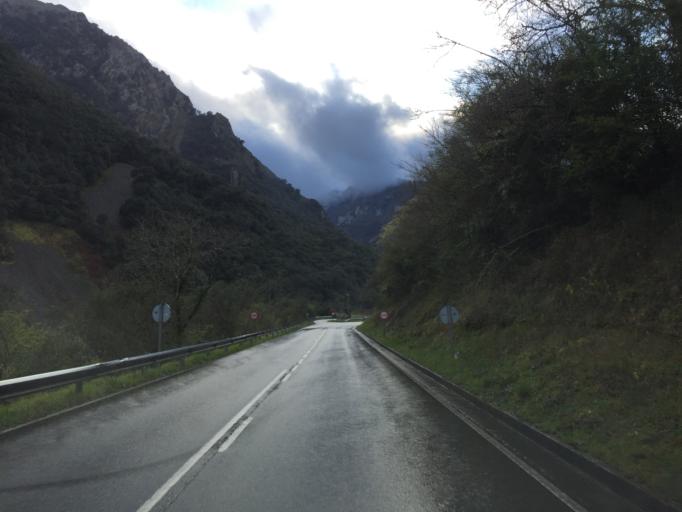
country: ES
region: Cantabria
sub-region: Provincia de Cantabria
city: Tresviso
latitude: 43.3157
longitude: -4.6993
